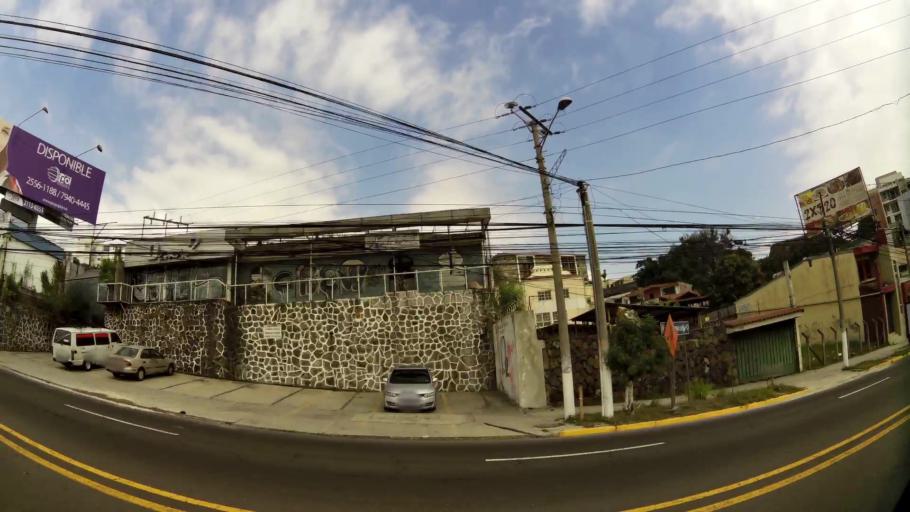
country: SV
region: La Libertad
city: Antiguo Cuscatlan
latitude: 13.7033
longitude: -89.2459
